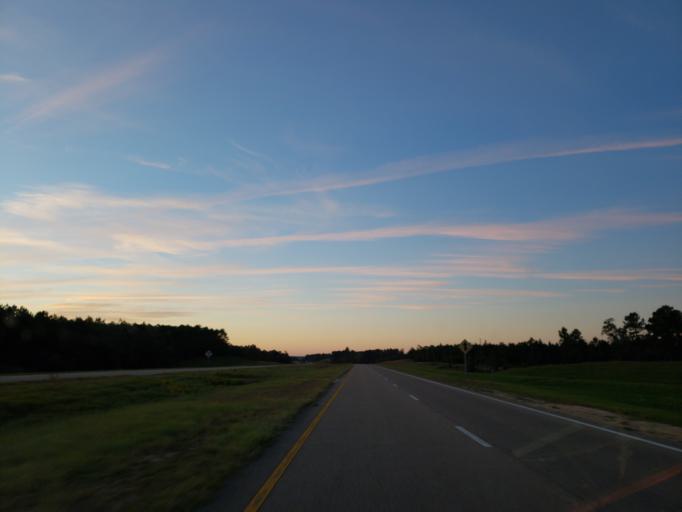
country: US
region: Mississippi
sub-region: Wayne County
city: Waynesboro
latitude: 31.7094
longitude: -88.6275
